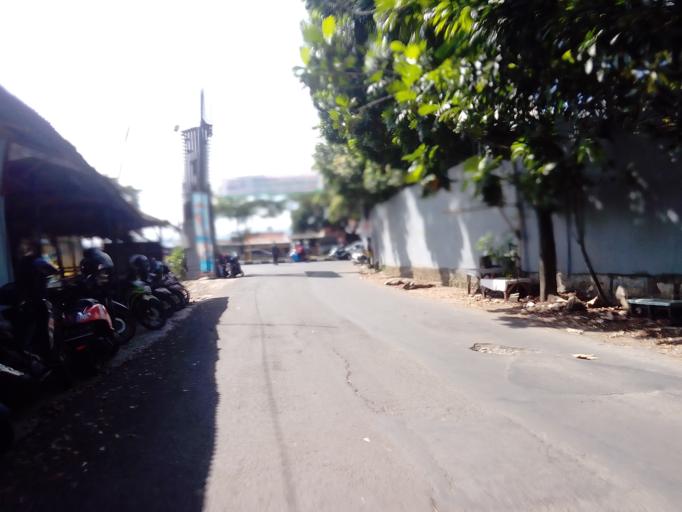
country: ID
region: West Java
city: Bandung
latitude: -6.9392
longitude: 107.6698
